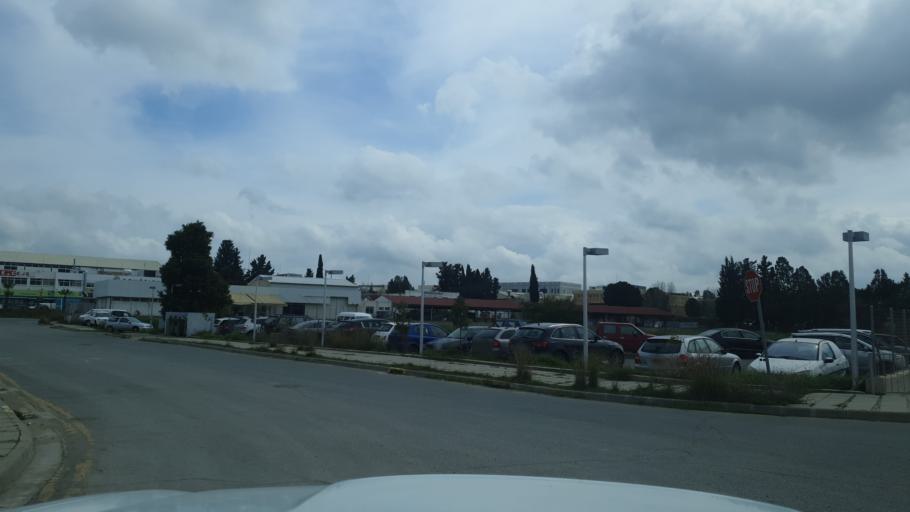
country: CY
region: Lefkosia
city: Geri
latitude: 35.0917
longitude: 33.3777
